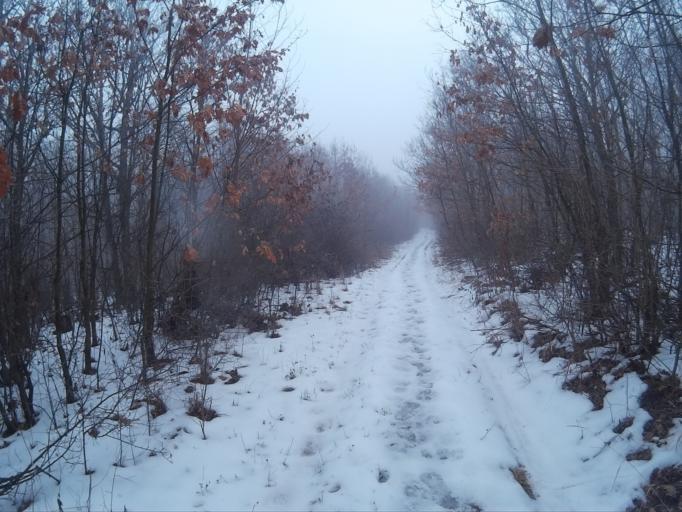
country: HU
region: Nograd
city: Matraverebely
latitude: 47.9861
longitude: 19.7618
